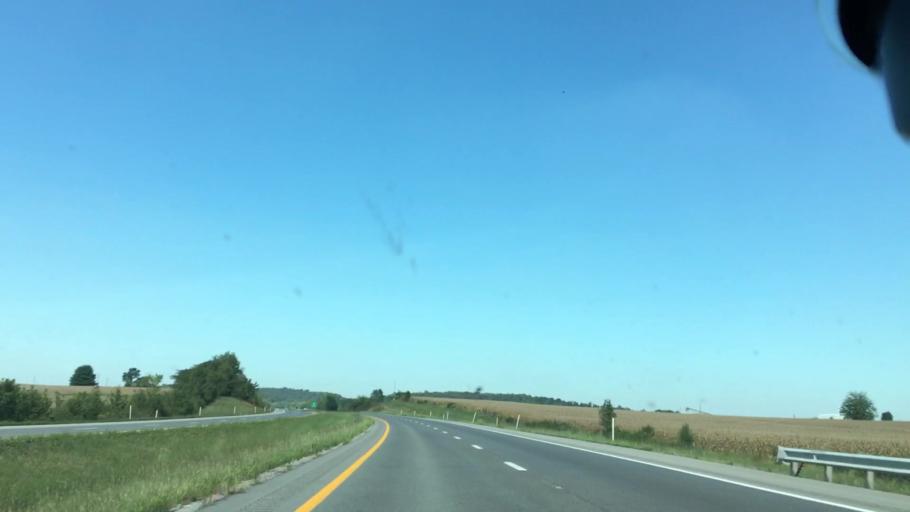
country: US
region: Kentucky
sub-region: Webster County
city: Sebree
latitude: 37.5733
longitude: -87.4793
